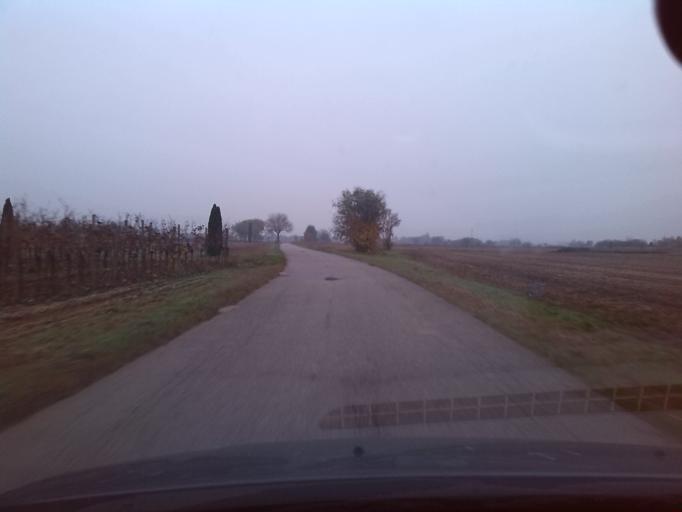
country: IT
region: Friuli Venezia Giulia
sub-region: Provincia di Gorizia
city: Moraro
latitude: 45.9122
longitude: 13.4870
